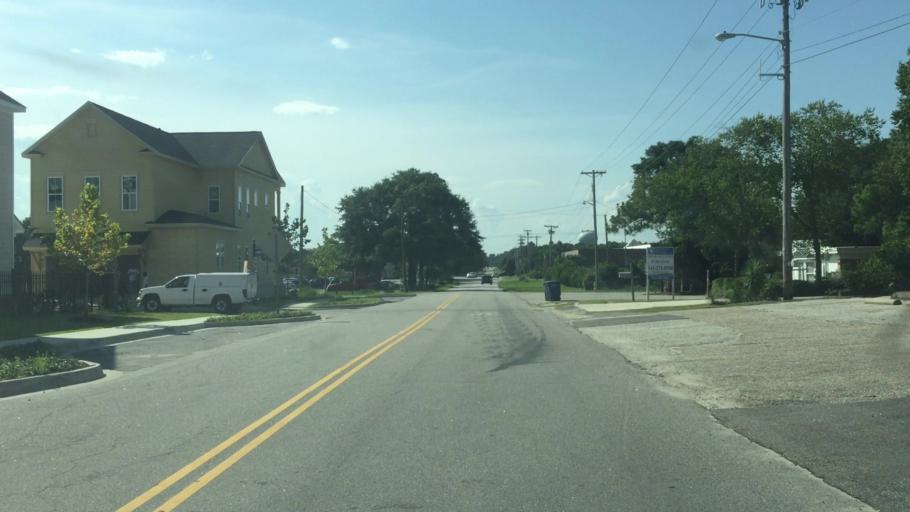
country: US
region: South Carolina
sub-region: Horry County
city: Myrtle Beach
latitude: 33.7473
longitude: -78.8141
